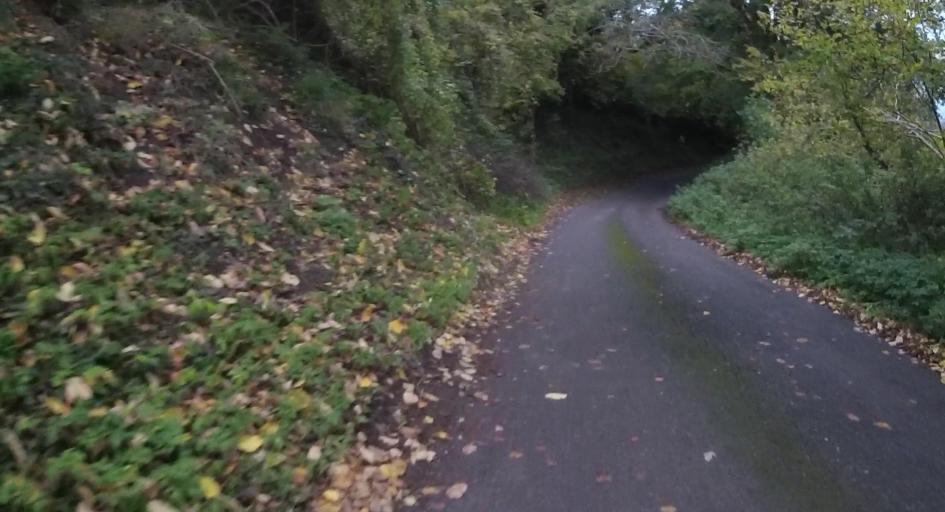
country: GB
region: England
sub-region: Hampshire
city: Kingsley
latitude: 51.1515
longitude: -0.8812
